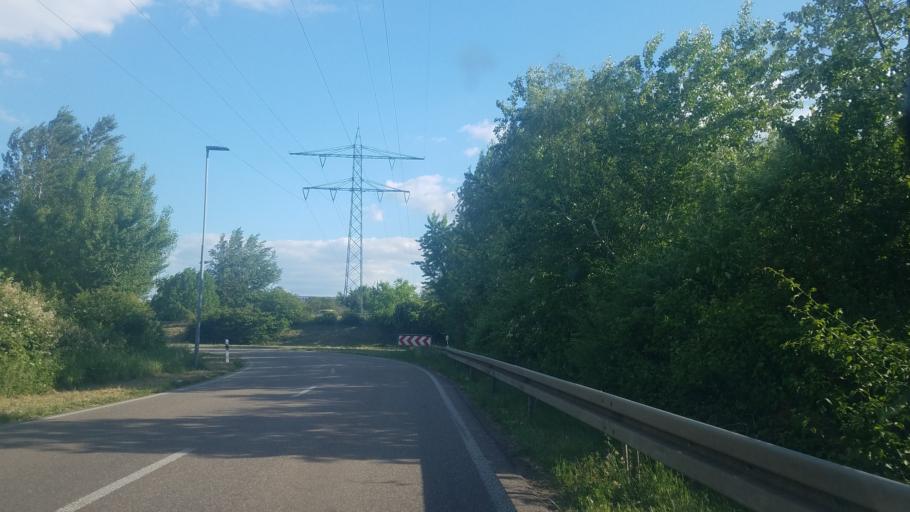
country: DE
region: Baden-Wuerttemberg
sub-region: Freiburg Region
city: Kehl
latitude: 48.5948
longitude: 7.8253
